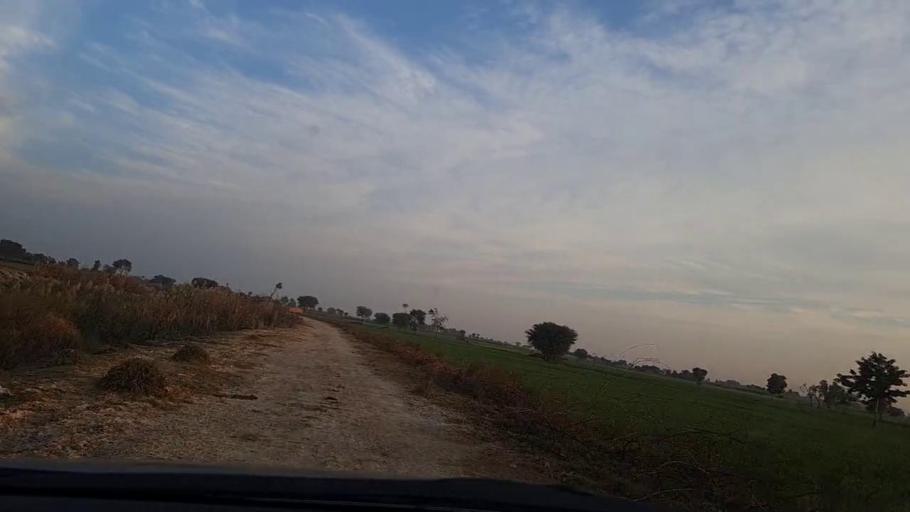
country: PK
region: Sindh
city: Sakrand
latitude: 26.1725
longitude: 68.3465
